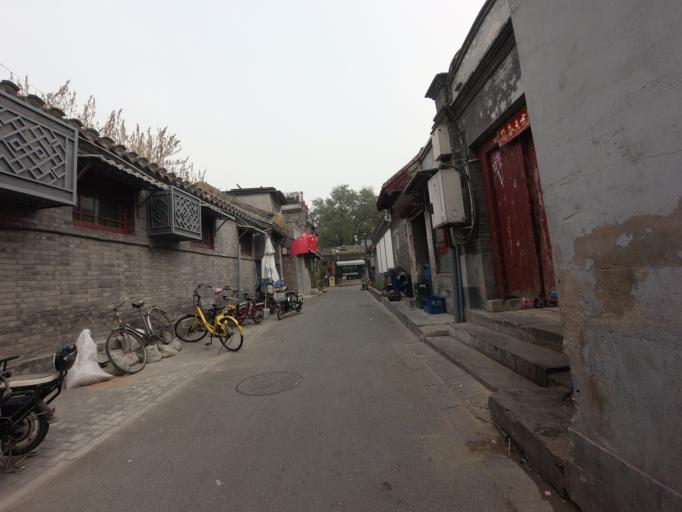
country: CN
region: Beijing
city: Jingshan
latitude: 39.9374
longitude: 116.3867
